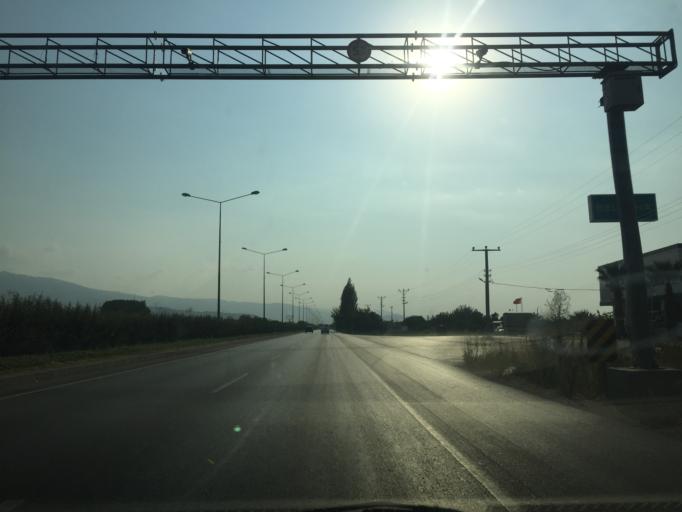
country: TR
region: Manisa
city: Salihli
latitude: 38.4940
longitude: 28.1763
